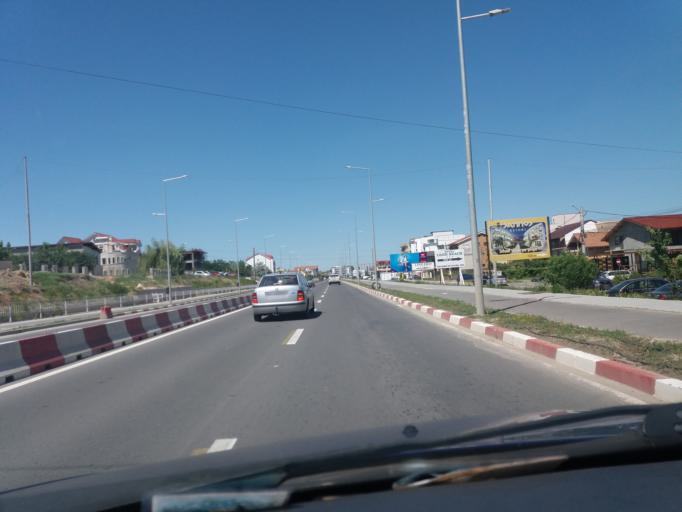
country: RO
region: Constanta
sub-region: Comuna Navodari
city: Navodari
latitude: 44.3027
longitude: 28.6202
